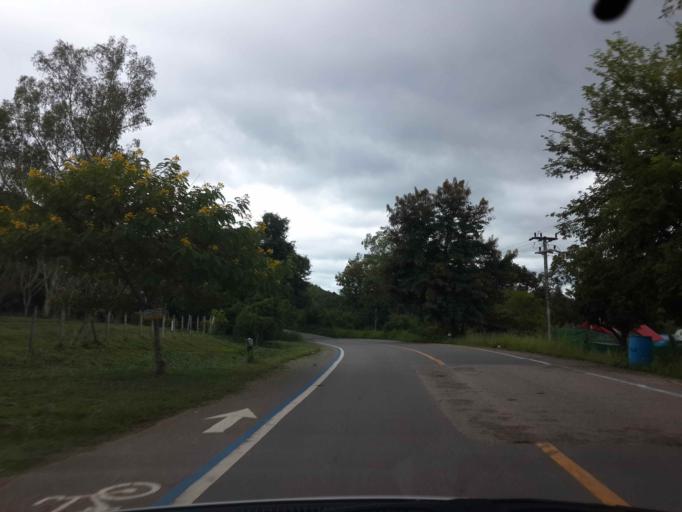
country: TH
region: Ratchaburi
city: Suan Phueng
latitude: 13.6362
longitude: 99.2163
